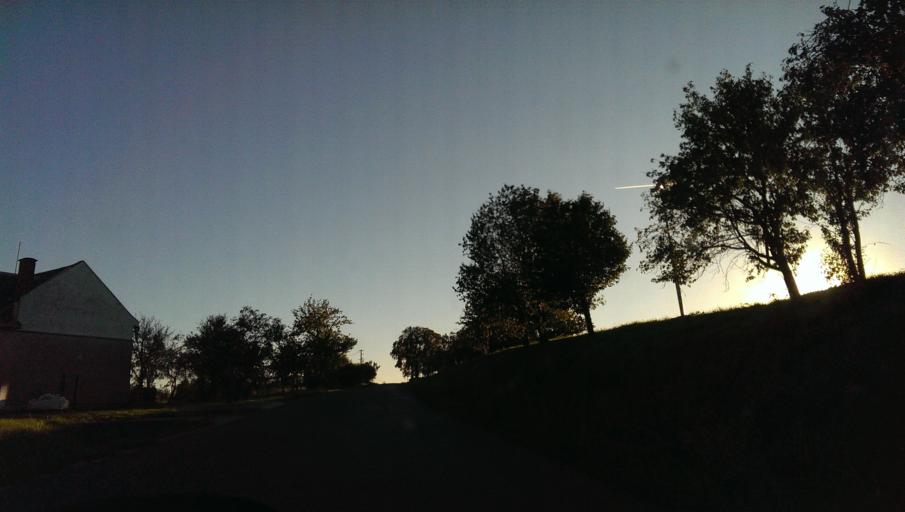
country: CZ
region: Zlin
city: Tupesy
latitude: 49.0885
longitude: 17.3745
